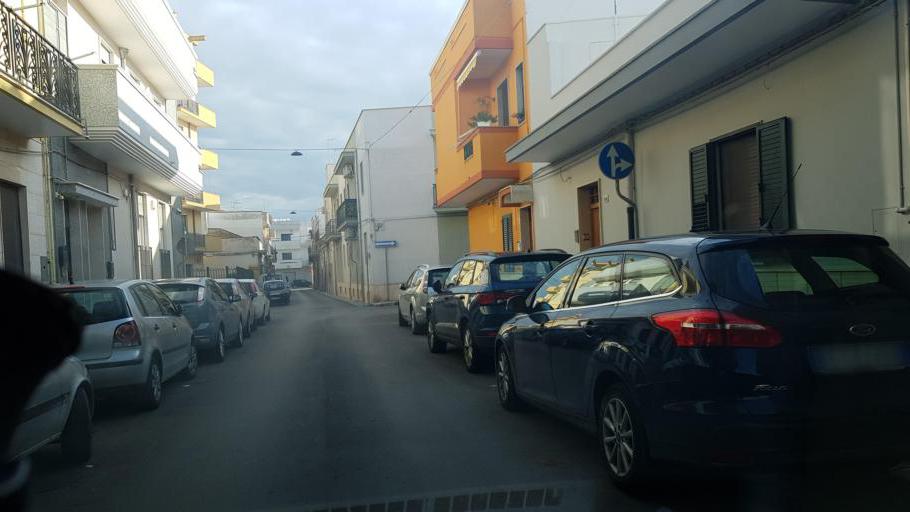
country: IT
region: Apulia
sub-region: Provincia di Brindisi
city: Francavilla Fontana
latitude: 40.5271
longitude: 17.5899
